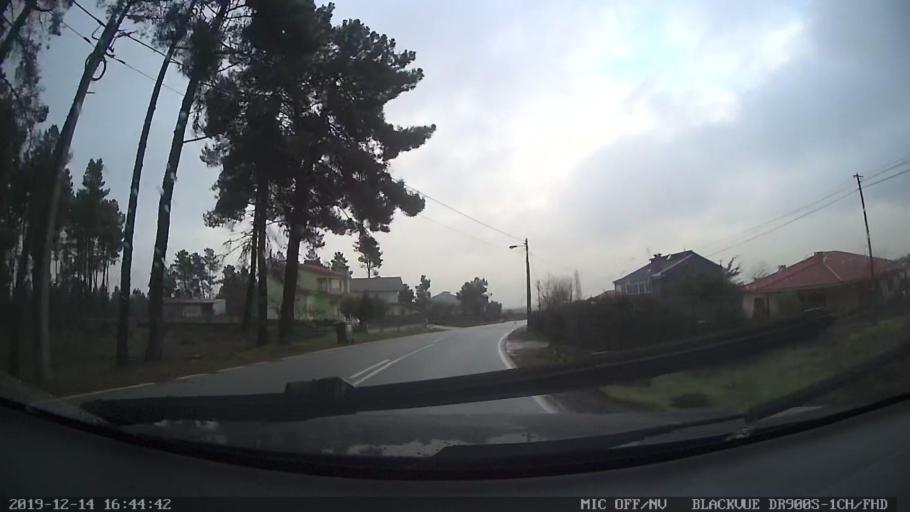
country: PT
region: Vila Real
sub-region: Murca
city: Murca
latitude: 41.3941
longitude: -7.4936
